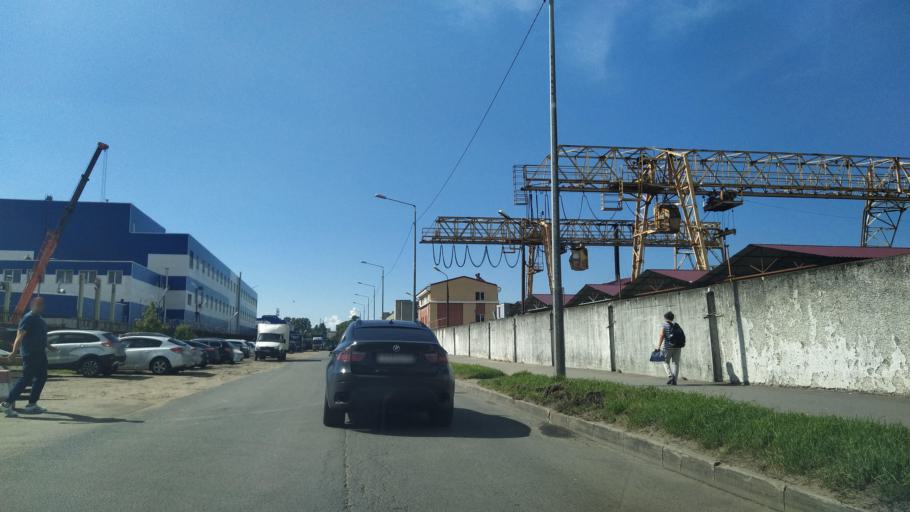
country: RU
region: Leningrad
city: Finlyandskiy
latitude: 59.9763
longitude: 30.3614
